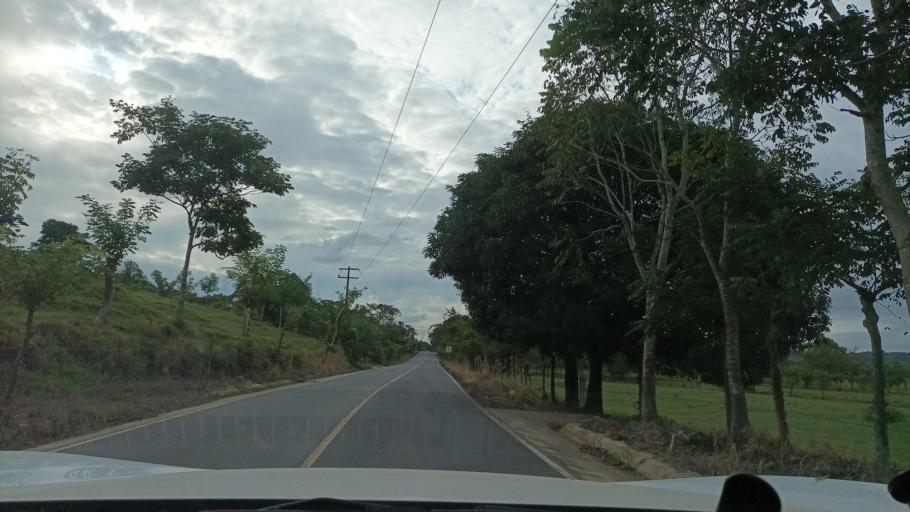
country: MX
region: Veracruz
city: Hidalgotitlan
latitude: 17.7423
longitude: -94.4905
